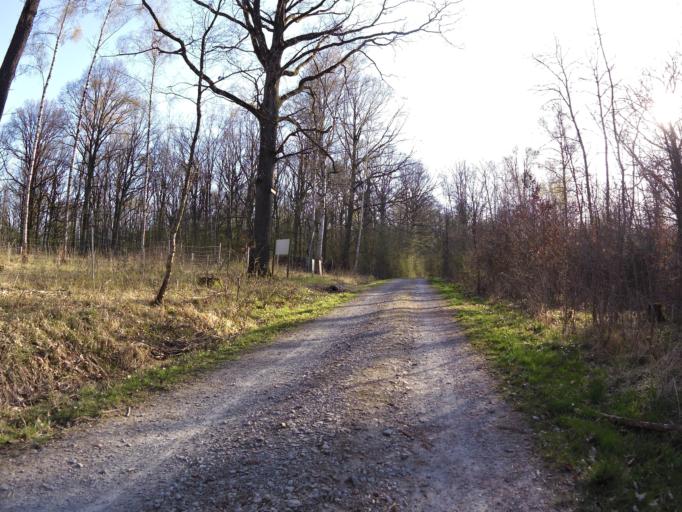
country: DE
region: Bavaria
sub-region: Regierungsbezirk Unterfranken
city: Kurnach
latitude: 49.8286
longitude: 10.0680
